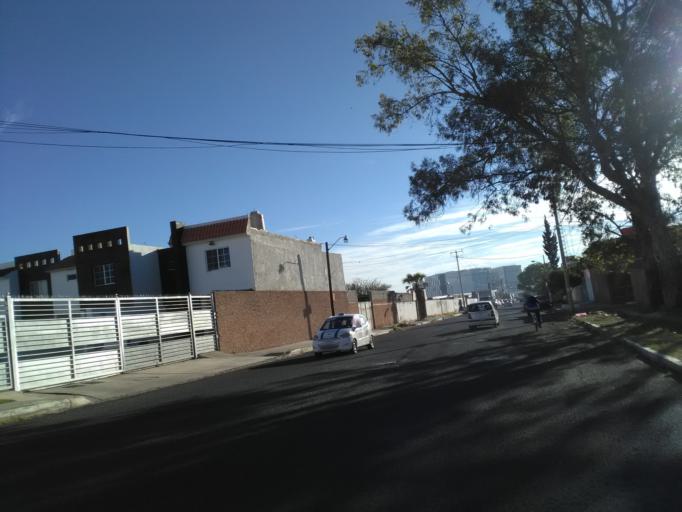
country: MX
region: Durango
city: Victoria de Durango
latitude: 24.0436
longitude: -104.6616
